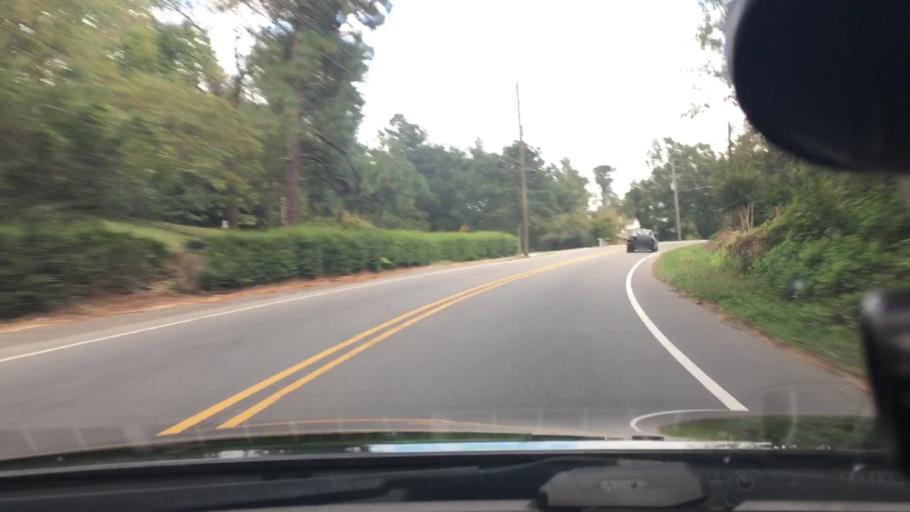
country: US
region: North Carolina
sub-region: Moore County
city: Carthage
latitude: 35.3549
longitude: -79.4242
